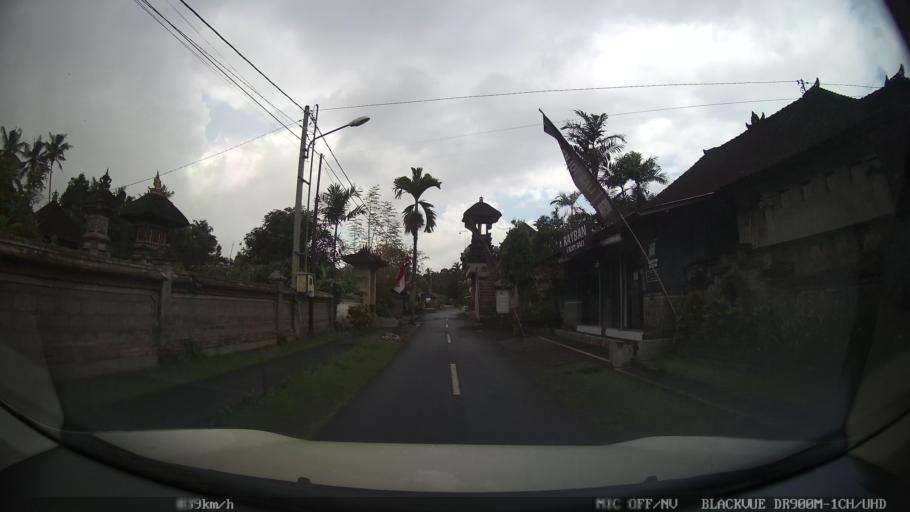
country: ID
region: Bali
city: Banjar Tebongkang
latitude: -8.5249
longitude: 115.2373
